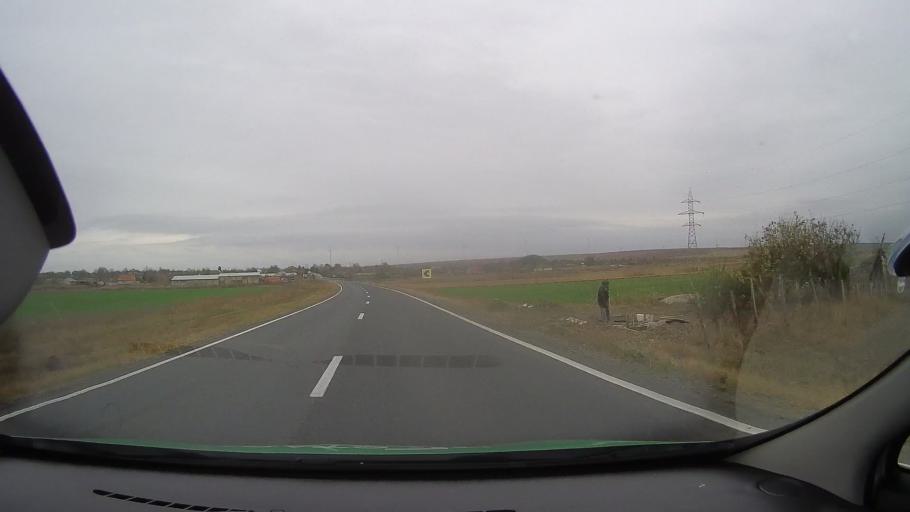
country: RO
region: Constanta
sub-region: Comuna Nicolae Balcescu
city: Dorobantu
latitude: 44.4142
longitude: 28.3177
